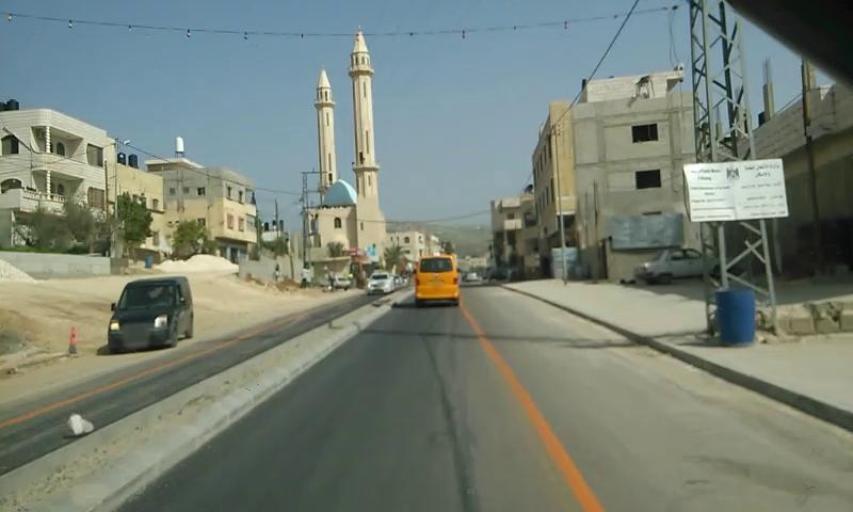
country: PS
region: West Bank
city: Huwwarah
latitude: 32.1570
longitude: 35.2599
